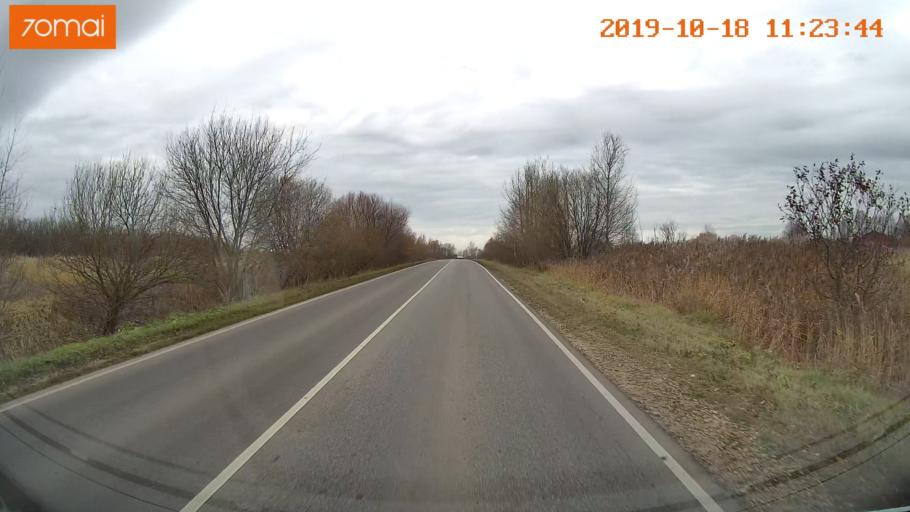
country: RU
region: Tula
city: Kimovsk
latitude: 54.1059
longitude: 38.5947
